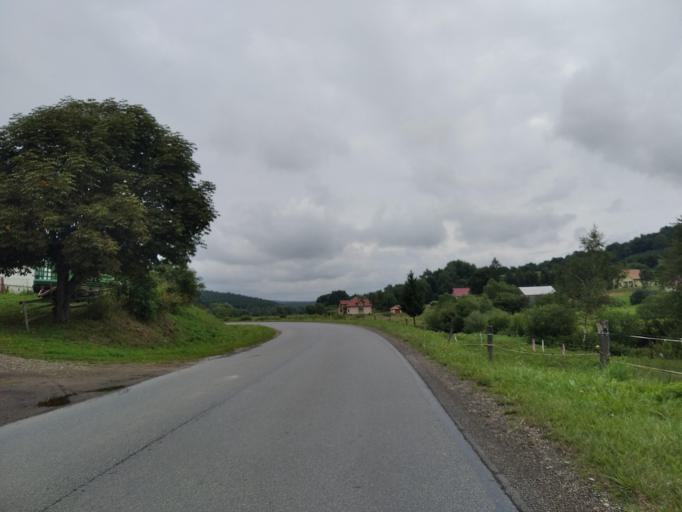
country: PL
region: Subcarpathian Voivodeship
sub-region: Powiat przemyski
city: Bircza
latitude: 49.6951
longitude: 22.3838
